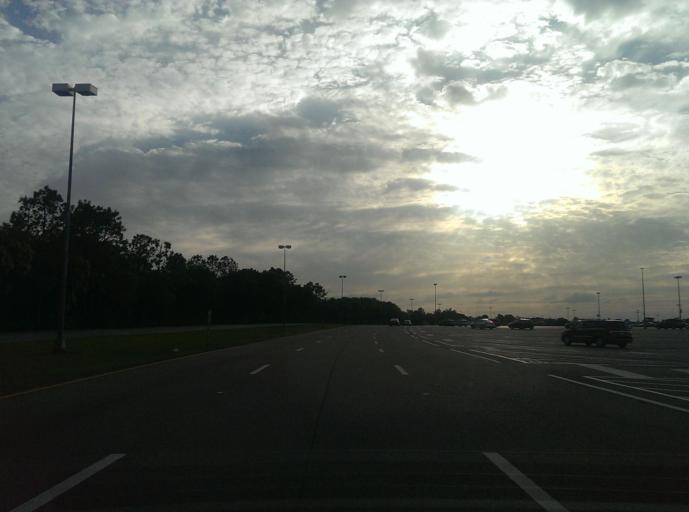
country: US
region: Florida
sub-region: Osceola County
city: Celebration
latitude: 28.3491
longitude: -81.5859
